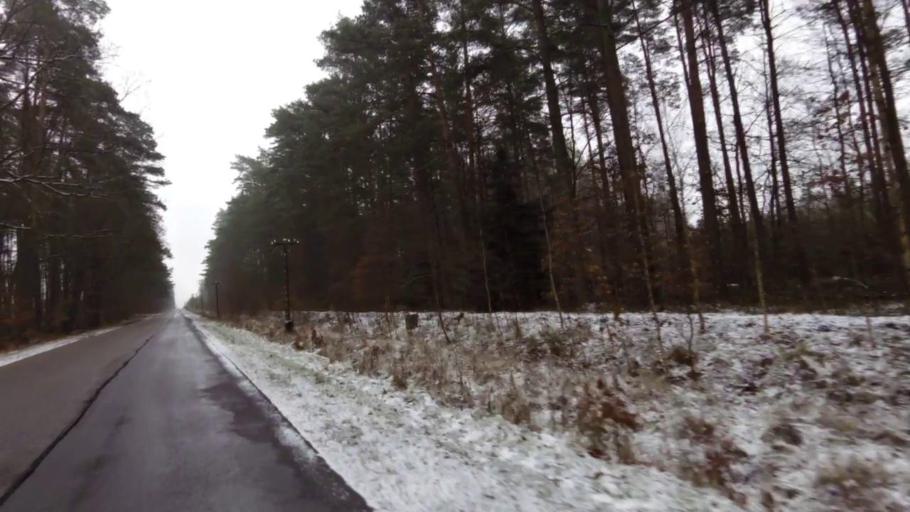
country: PL
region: West Pomeranian Voivodeship
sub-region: Powiat drawski
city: Czaplinek
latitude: 53.4431
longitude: 16.2240
